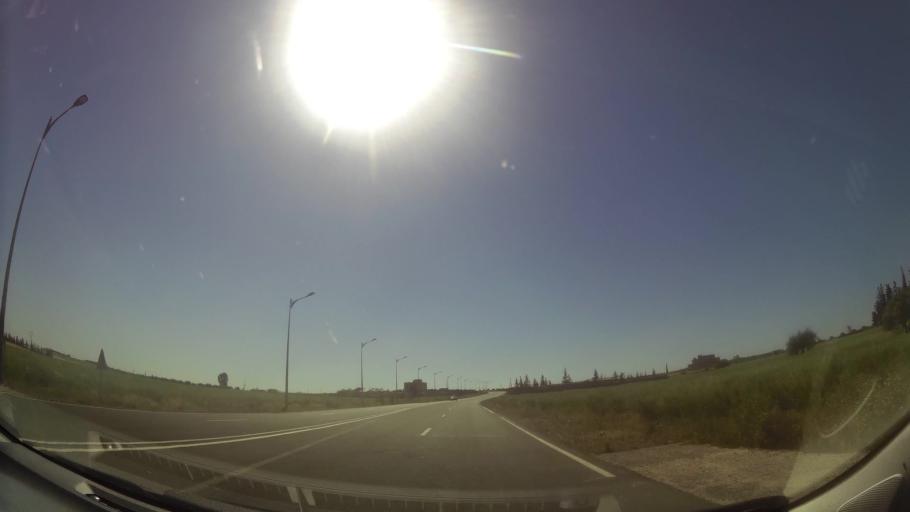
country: MA
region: Oriental
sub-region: Oujda-Angad
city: Oujda
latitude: 34.7402
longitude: -1.8973
